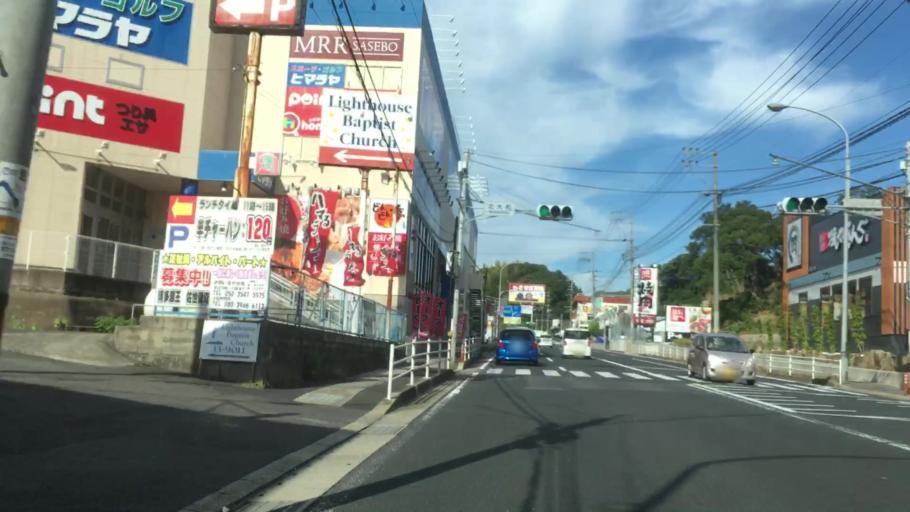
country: JP
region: Nagasaki
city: Sasebo
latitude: 33.1610
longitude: 129.7492
